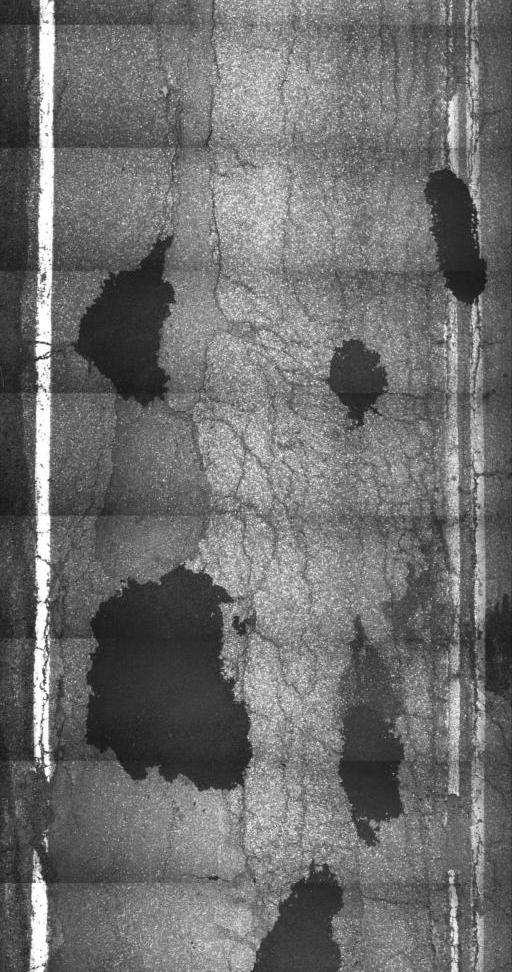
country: US
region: Vermont
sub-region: Orange County
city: Randolph
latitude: 43.9803
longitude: -72.6483
